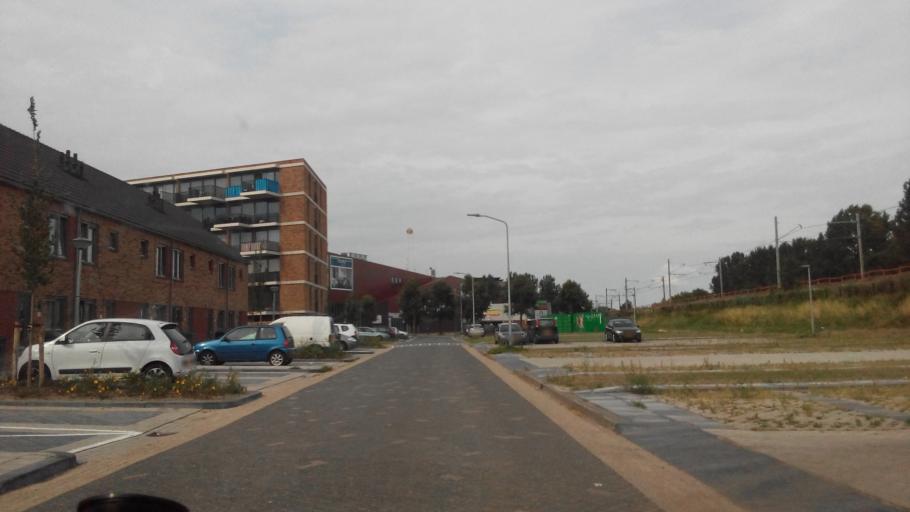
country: NL
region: Flevoland
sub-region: Gemeente Almere
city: Almere Stad
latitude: 52.3905
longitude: 5.2721
